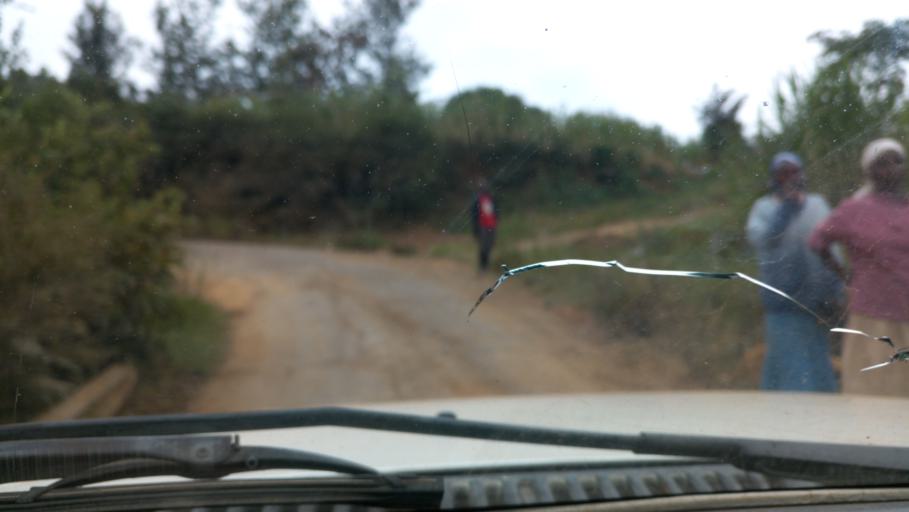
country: KE
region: Murang'a District
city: Murang'a
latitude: -0.7093
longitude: 37.1230
